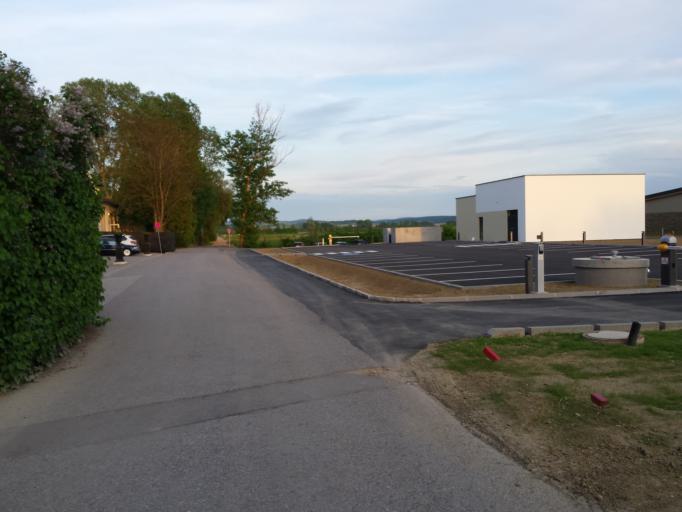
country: AT
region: Lower Austria
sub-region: Politischer Bezirk Tulln
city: Atzenbrugg
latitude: 48.3148
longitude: 15.9036
